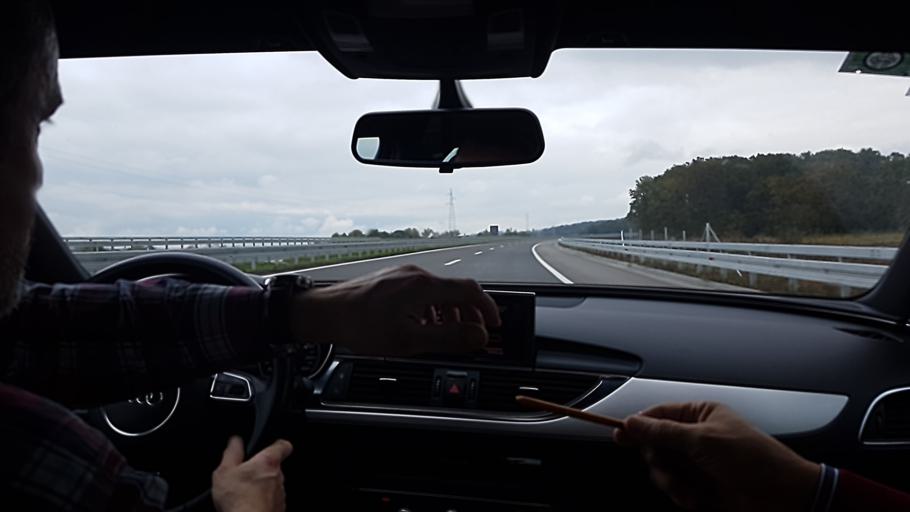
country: BA
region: Republika Srpska
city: Prnjavor
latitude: 44.8553
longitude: 17.6968
